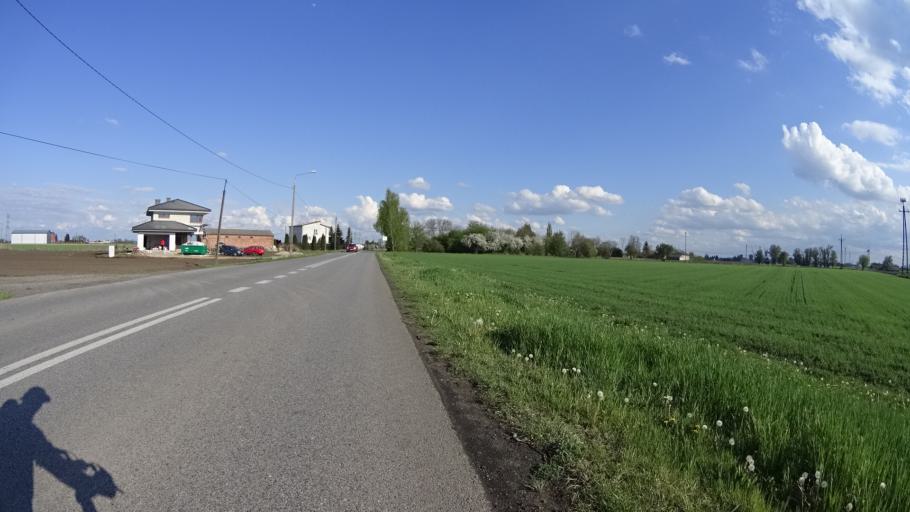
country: PL
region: Masovian Voivodeship
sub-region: Powiat warszawski zachodni
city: Jozefow
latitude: 52.2340
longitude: 20.7294
